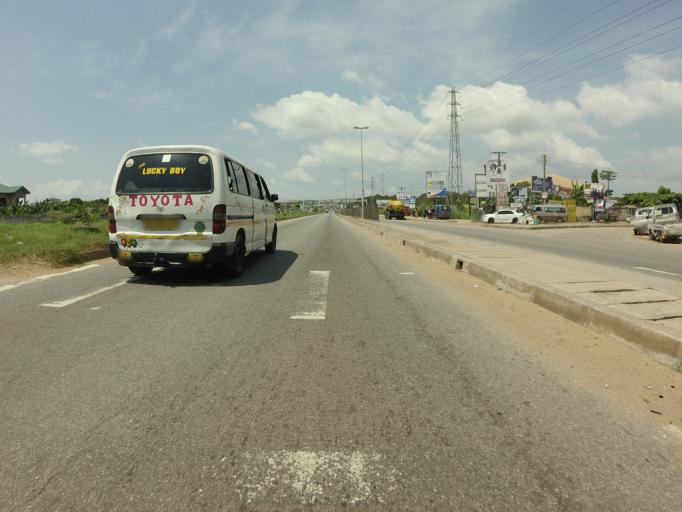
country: GH
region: Greater Accra
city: Gbawe
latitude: 5.5890
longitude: -0.2824
